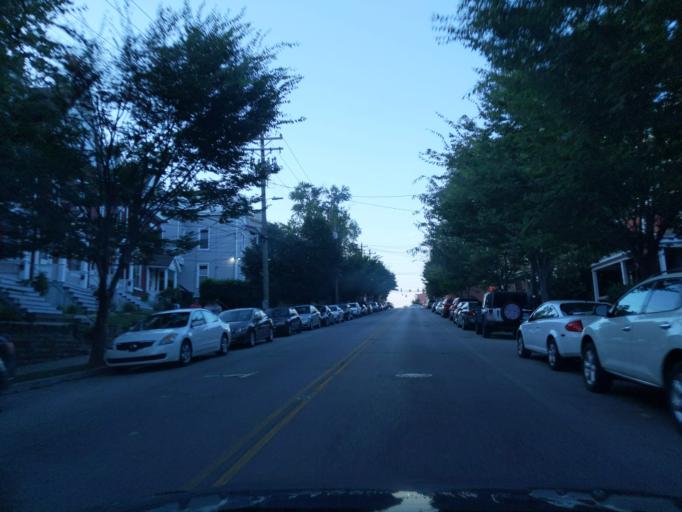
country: US
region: Kentucky
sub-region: Campbell County
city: Newport
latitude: 39.1262
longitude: -84.5196
